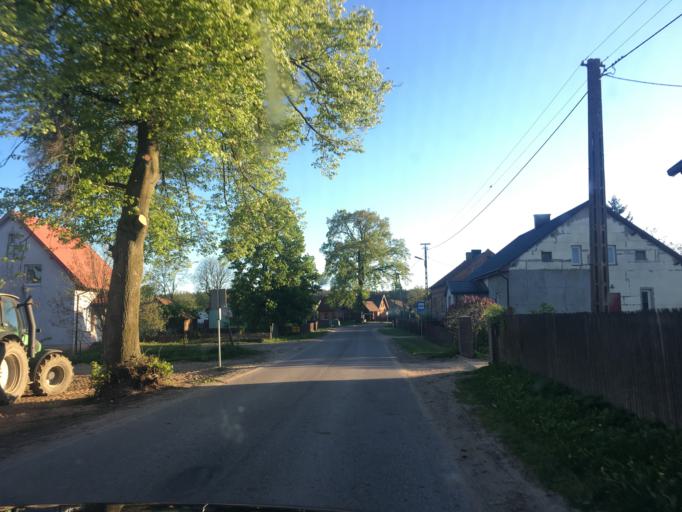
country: PL
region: Warmian-Masurian Voivodeship
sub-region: Powiat mragowski
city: Piecki
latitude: 53.7003
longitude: 21.3006
